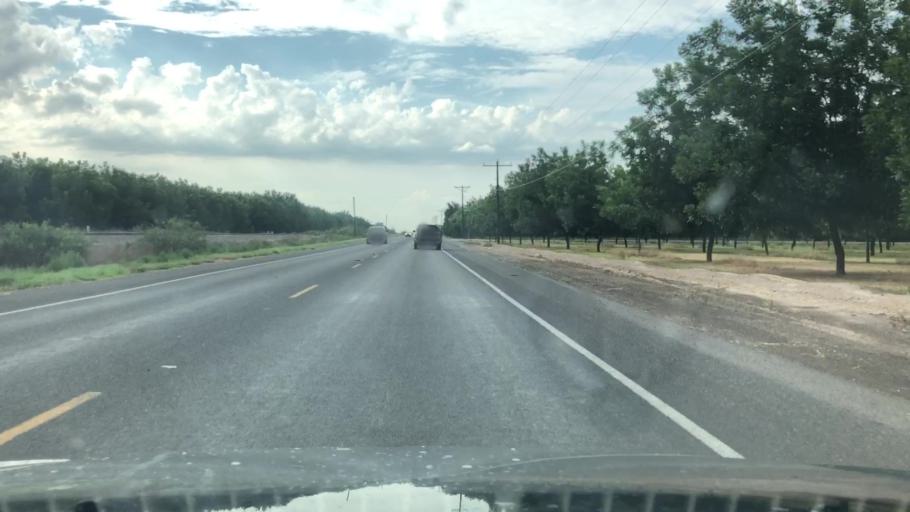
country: US
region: New Mexico
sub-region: Dona Ana County
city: Mesquite
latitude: 32.2147
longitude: -106.7281
